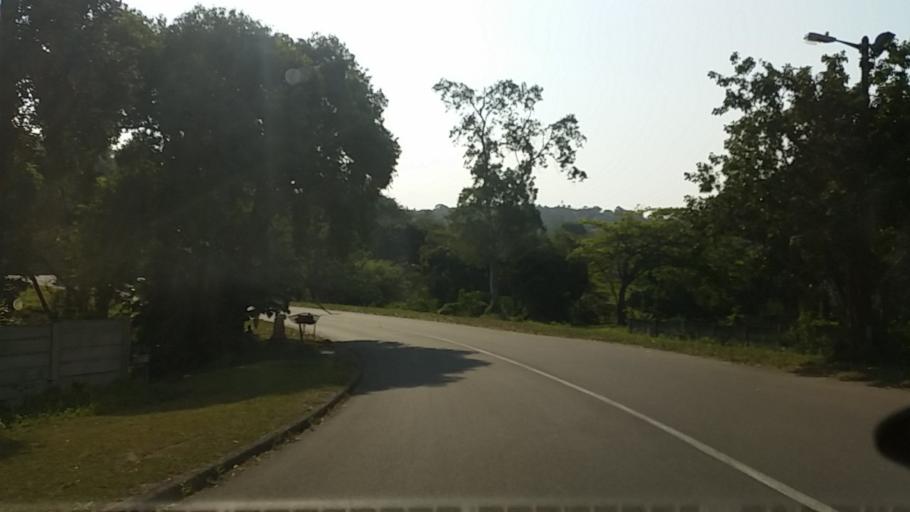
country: ZA
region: KwaZulu-Natal
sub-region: eThekwini Metropolitan Municipality
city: Berea
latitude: -29.8394
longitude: 30.9518
